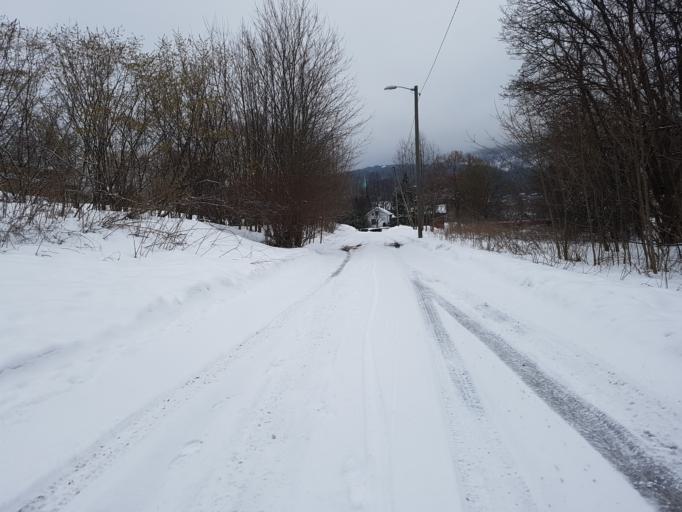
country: NO
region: Buskerud
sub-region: Drammen
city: Drammen
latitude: 59.7398
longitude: 10.1868
